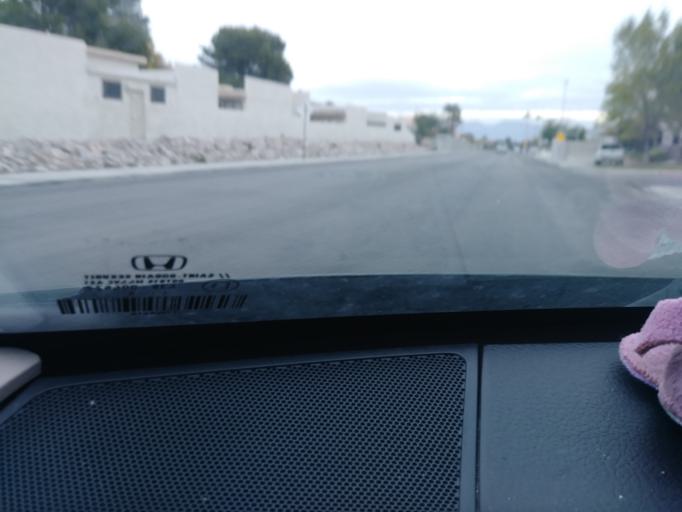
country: US
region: Nevada
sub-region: Clark County
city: Spring Valley
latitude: 36.1770
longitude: -115.2186
